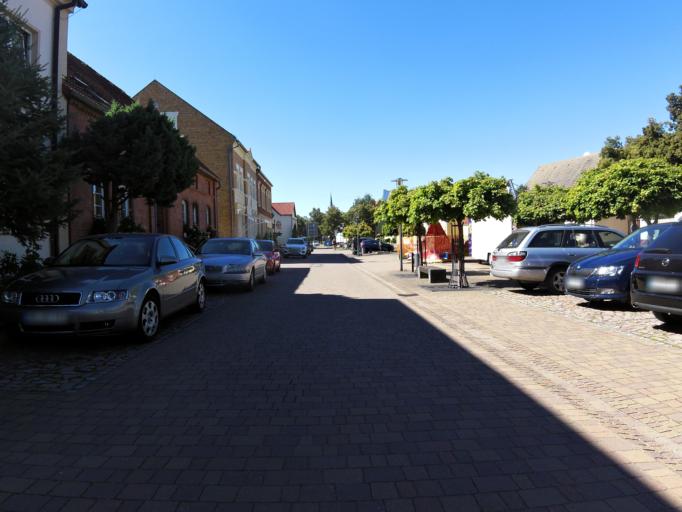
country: DE
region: Saxony-Anhalt
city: Elster
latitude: 51.8274
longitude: 12.8265
